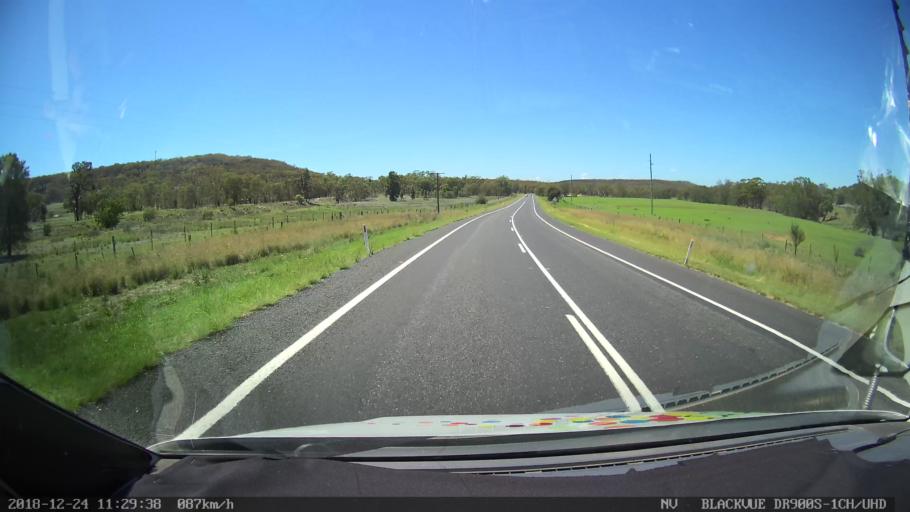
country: AU
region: New South Wales
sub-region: Upper Hunter Shire
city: Merriwa
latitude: -32.1949
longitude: 150.4638
